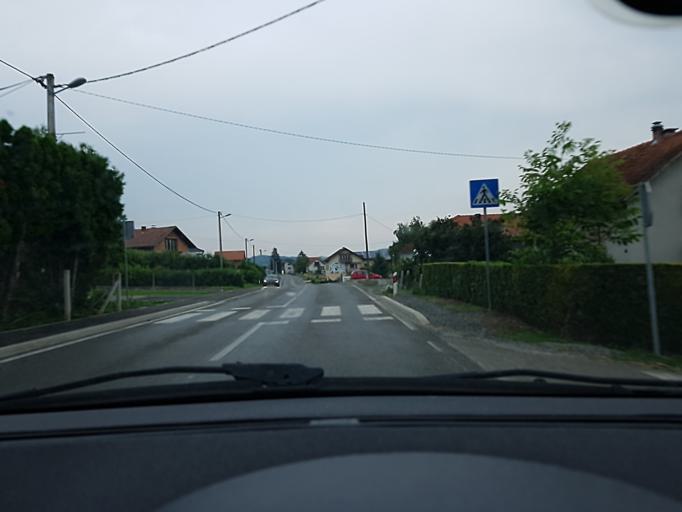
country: HR
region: Zagrebacka
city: Jakovlje
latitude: 46.0062
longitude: 15.8515
